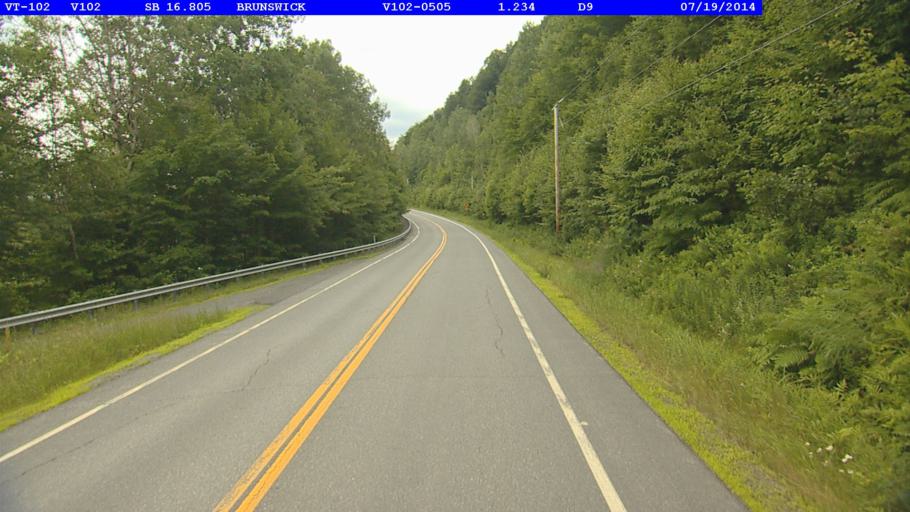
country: US
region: New Hampshire
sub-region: Coos County
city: Stratford
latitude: 44.6778
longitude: -71.5974
